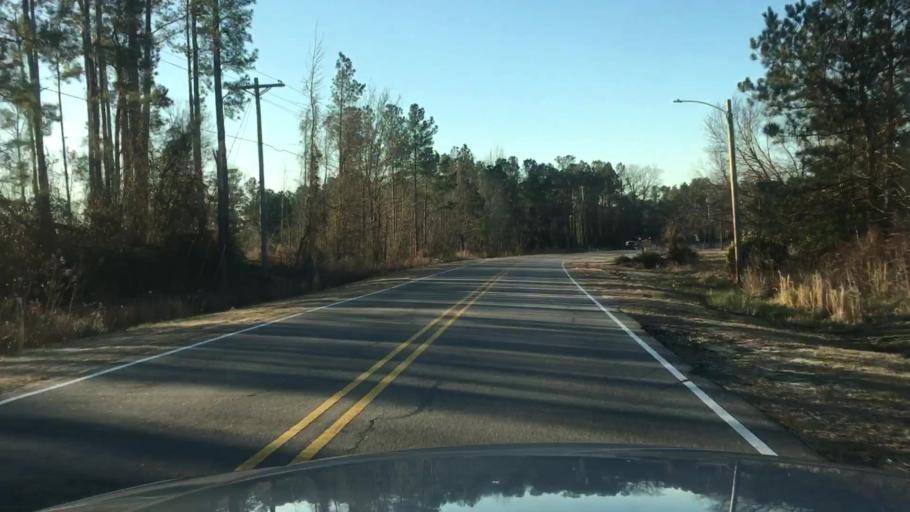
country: US
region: North Carolina
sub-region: Cumberland County
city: Hope Mills
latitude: 34.9659
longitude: -79.0079
